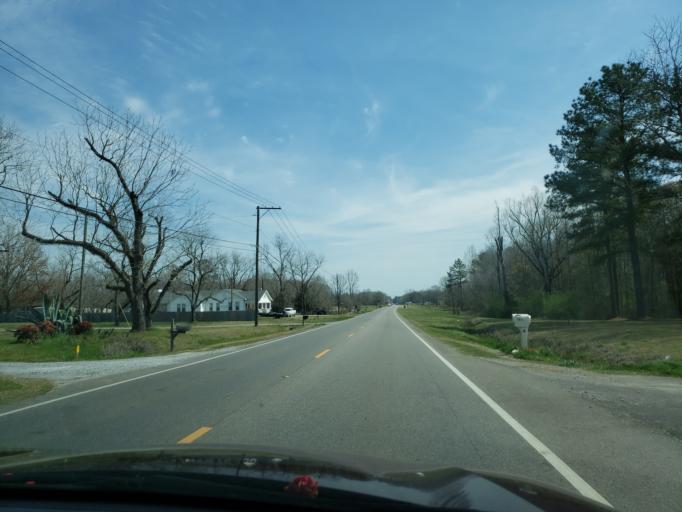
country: US
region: Alabama
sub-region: Autauga County
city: Prattville
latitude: 32.4307
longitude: -86.5177
